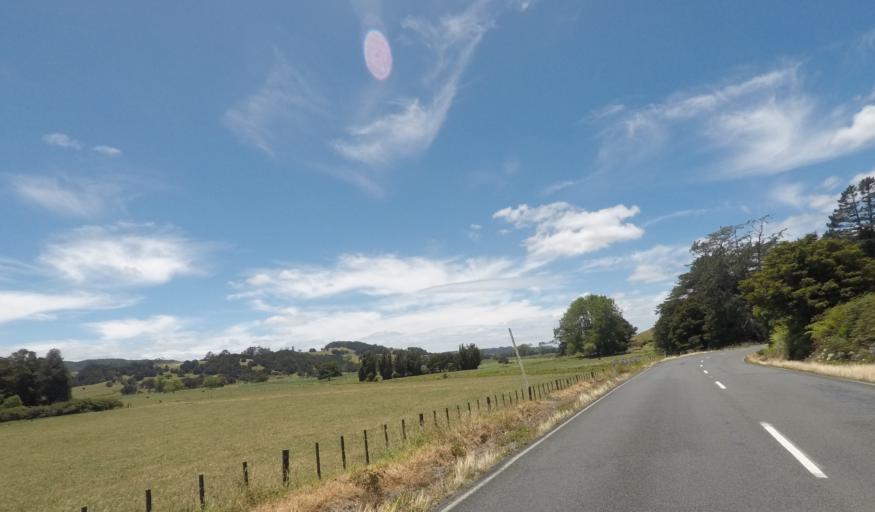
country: NZ
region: Northland
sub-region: Whangarei
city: Whangarei
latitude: -35.5370
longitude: 174.3108
